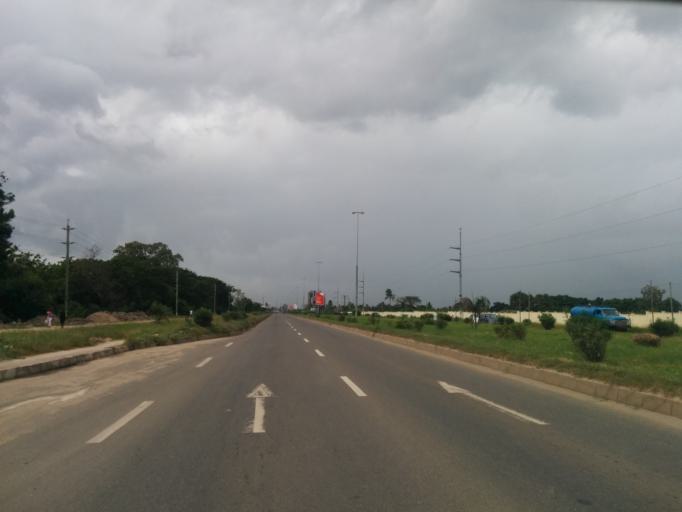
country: TZ
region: Dar es Salaam
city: Magomeni
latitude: -6.7827
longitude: 39.2144
